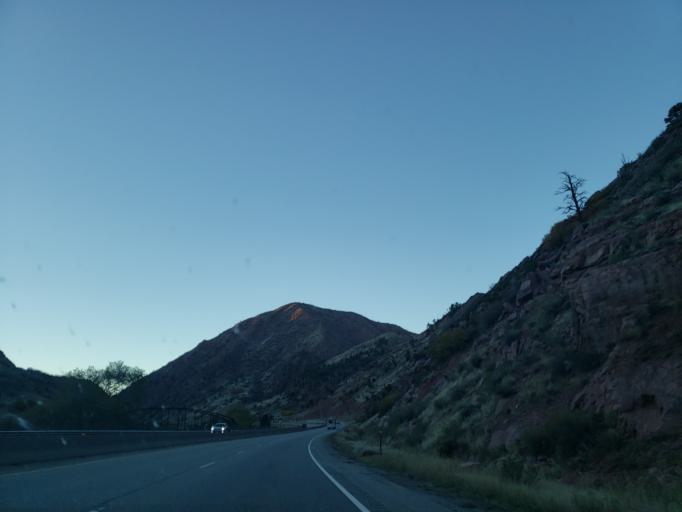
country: US
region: Colorado
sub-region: Garfield County
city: Glenwood Springs
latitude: 39.5607
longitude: -107.4053
